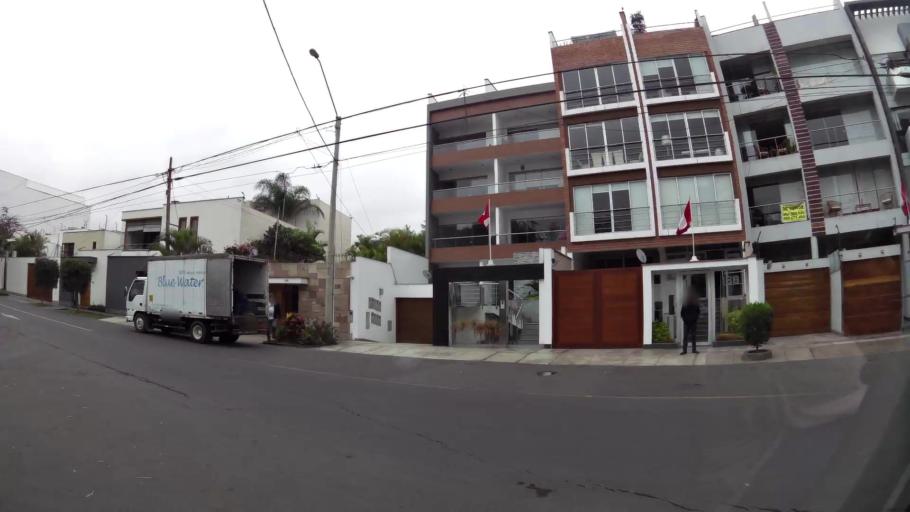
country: PE
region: Lima
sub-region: Lima
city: Surco
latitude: -12.1220
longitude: -77.0104
